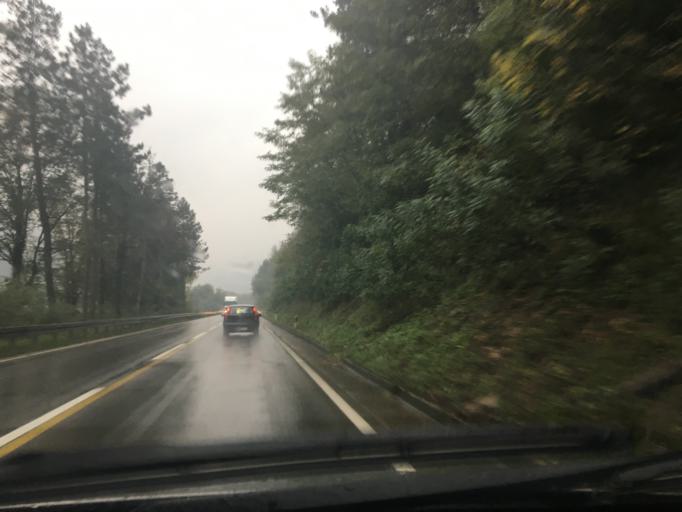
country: RS
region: Central Serbia
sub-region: Pcinjski Okrug
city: Vladicin Han
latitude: 42.8202
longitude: 22.1243
